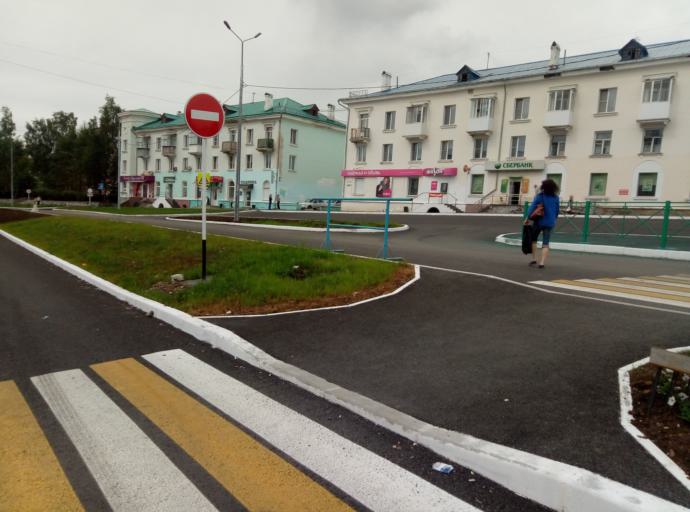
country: RU
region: Sverdlovsk
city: Krasnotur'insk
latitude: 59.7636
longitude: 60.2006
